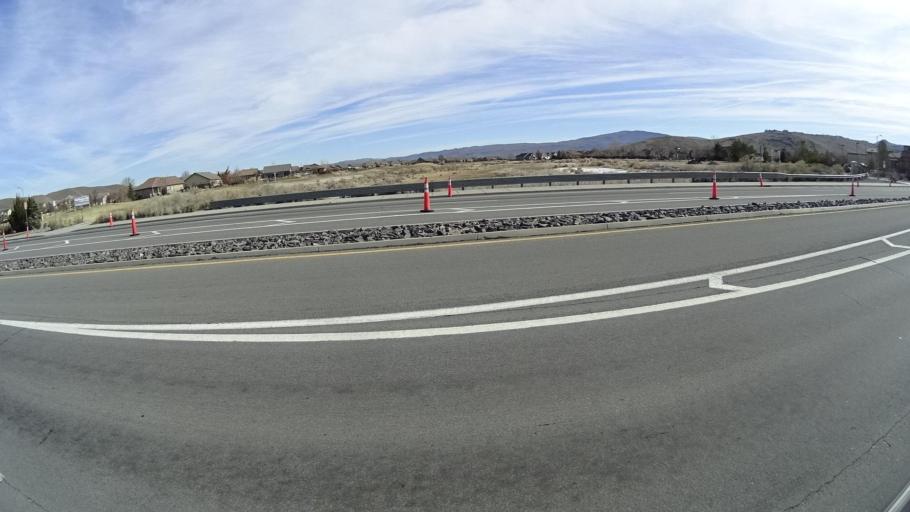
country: US
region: Nevada
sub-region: Washoe County
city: Sun Valley
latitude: 39.5900
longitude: -119.7291
